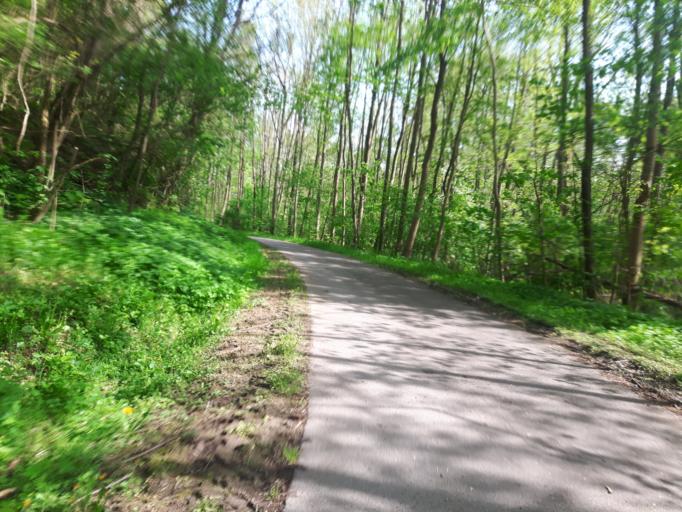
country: DE
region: Baden-Wuerttemberg
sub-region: Karlsruhe Region
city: Muhlhausen
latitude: 49.2483
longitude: 8.7452
